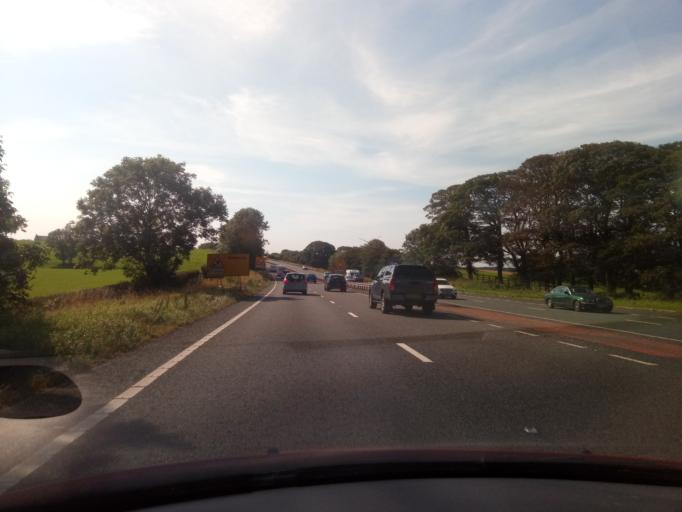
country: GB
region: England
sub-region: Hartlepool
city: Elwick
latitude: 54.6634
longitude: -1.3024
